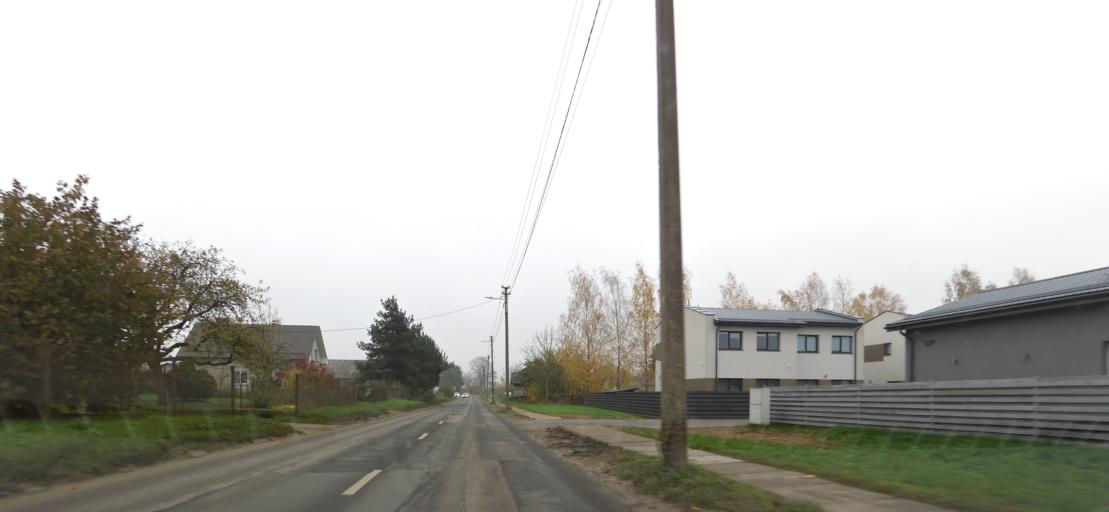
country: LT
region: Vilnius County
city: Rasos
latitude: 54.6608
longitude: 25.3525
